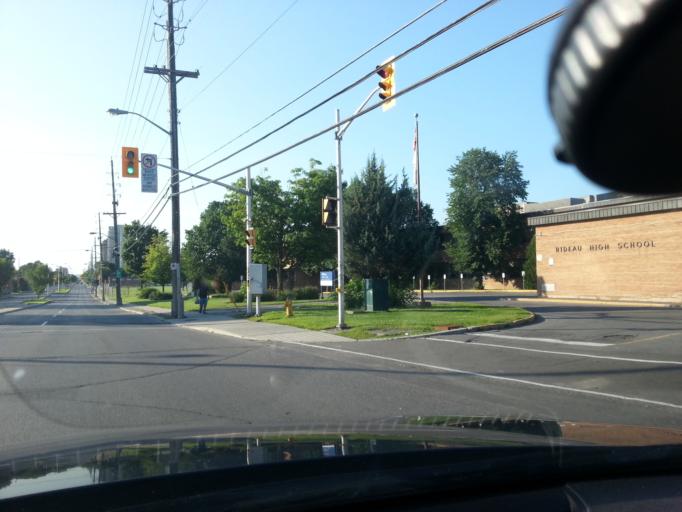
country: CA
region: Ontario
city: Ottawa
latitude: 45.4340
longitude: -75.6428
